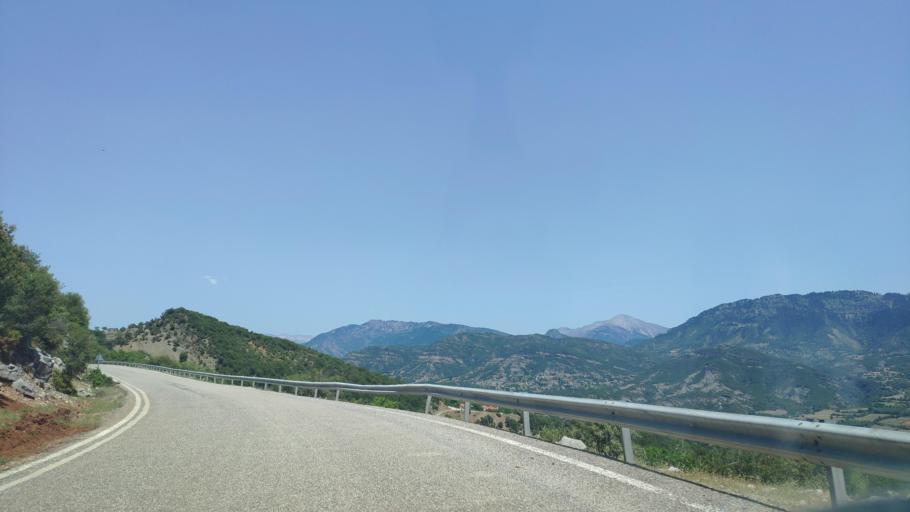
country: GR
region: Central Greece
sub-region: Nomos Evrytanias
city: Kerasochori
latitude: 39.0996
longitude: 21.4121
